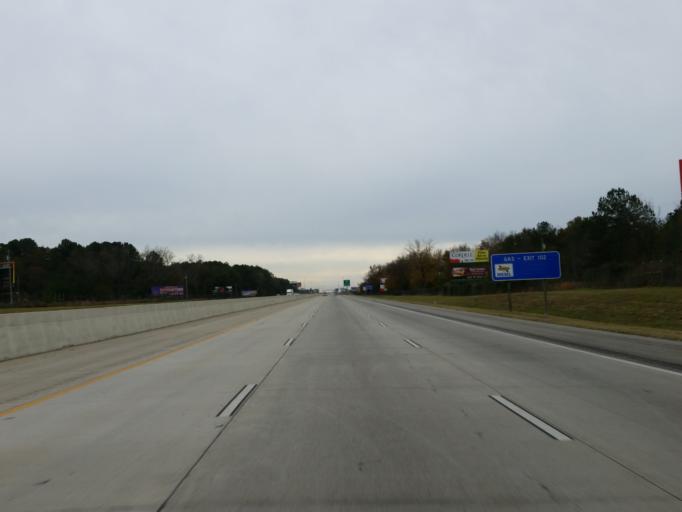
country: US
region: Georgia
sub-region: Crisp County
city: Cordele
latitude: 31.9929
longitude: -83.7569
